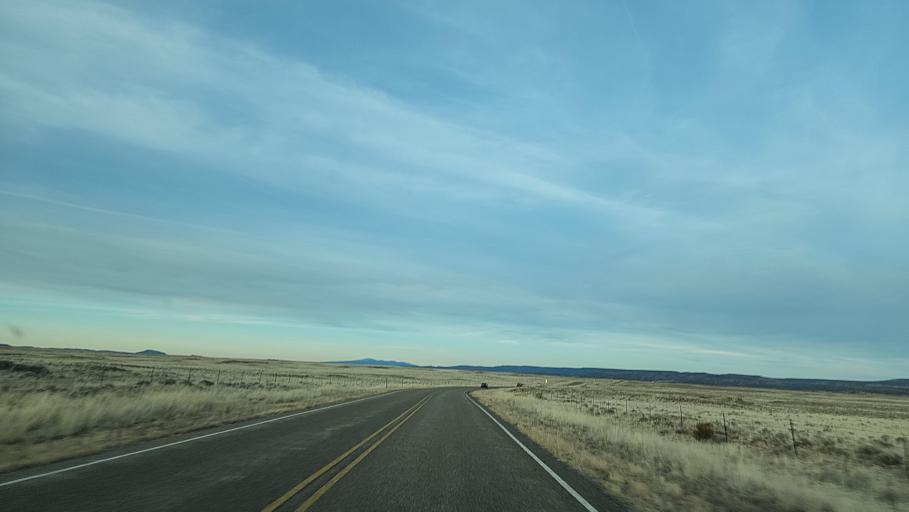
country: US
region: New Mexico
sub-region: Cibola County
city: Grants
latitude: 34.6808
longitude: -108.0758
